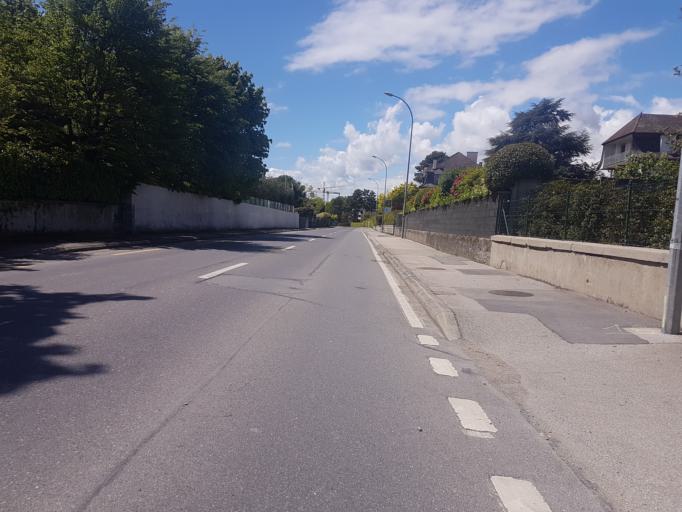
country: CH
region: Vaud
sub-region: Nyon District
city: Prangins
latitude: 46.3888
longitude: 6.2490
